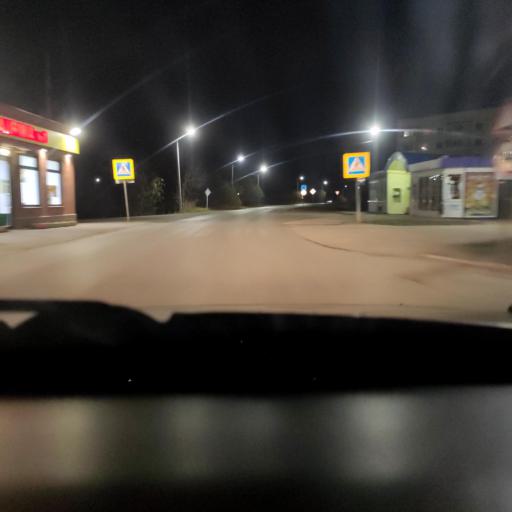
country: RU
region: Perm
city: Kondratovo
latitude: 57.9762
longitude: 56.1090
